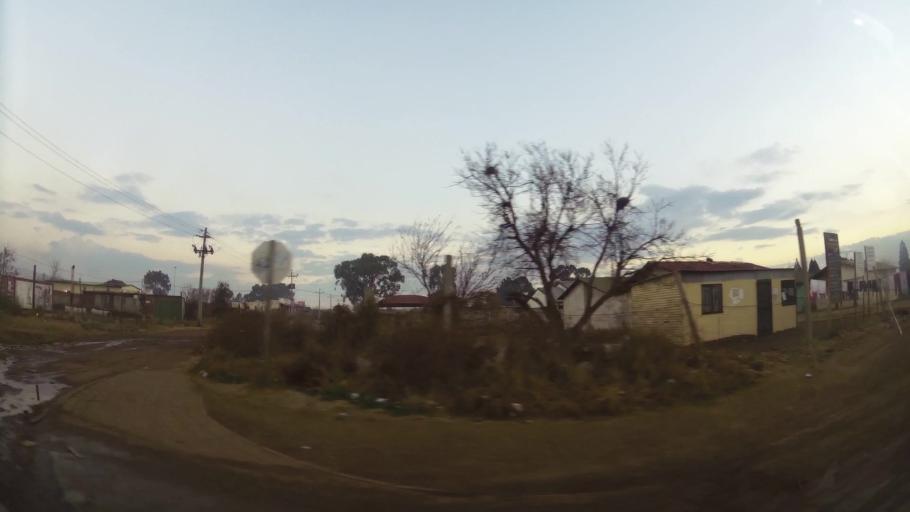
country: ZA
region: Gauteng
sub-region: City of Johannesburg Metropolitan Municipality
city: Orange Farm
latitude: -26.5481
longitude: 27.8529
